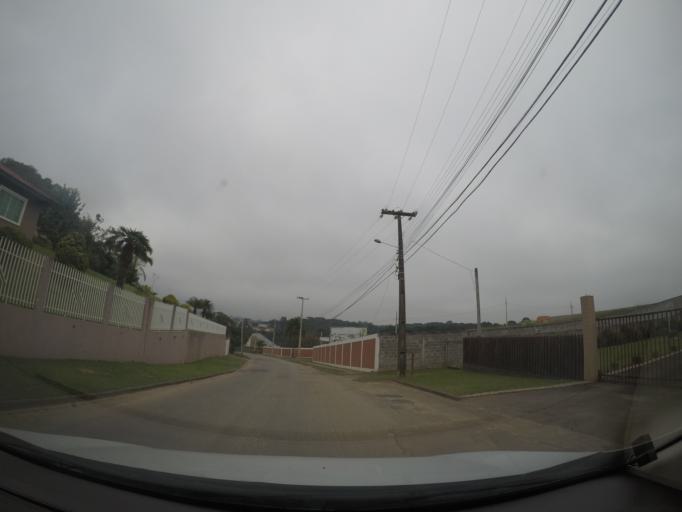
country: BR
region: Parana
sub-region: Colombo
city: Colombo
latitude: -25.3291
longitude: -49.2510
